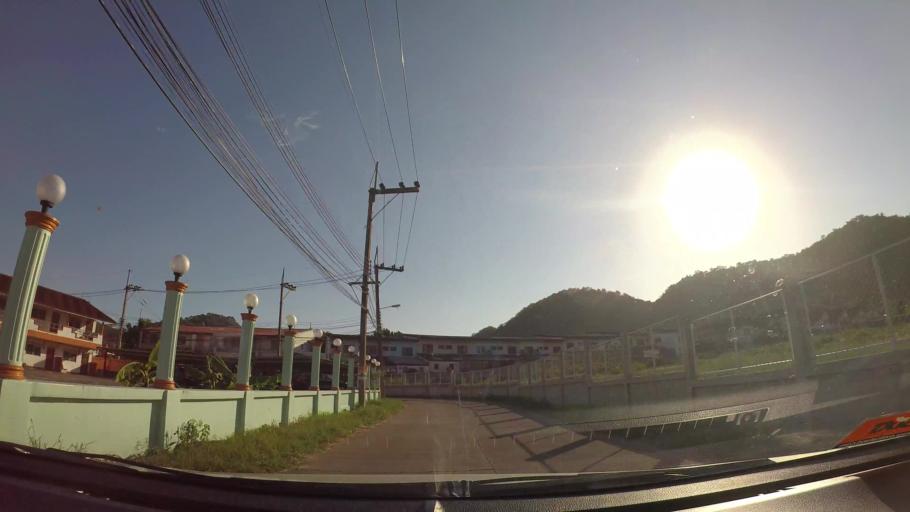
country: TH
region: Chon Buri
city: Si Racha
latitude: 13.1484
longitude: 100.9318
